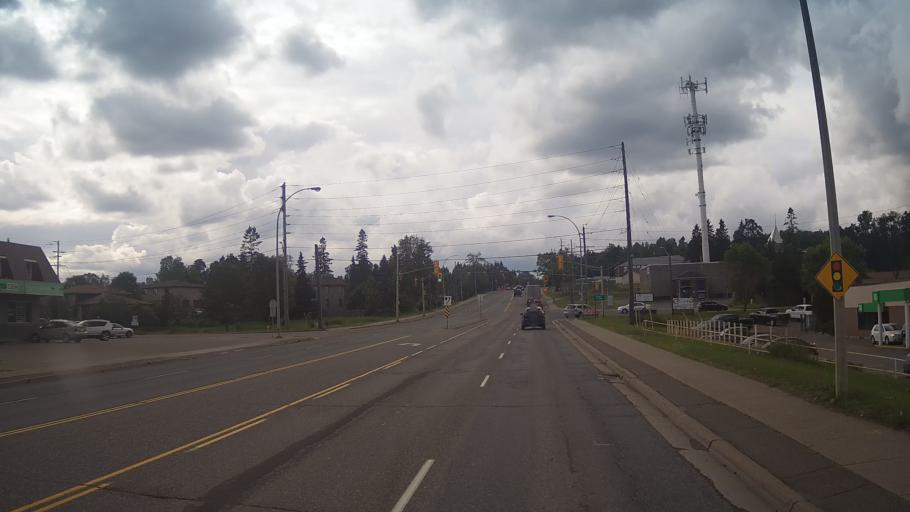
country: CA
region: Ontario
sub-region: Thunder Bay District
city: Thunder Bay
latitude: 48.4522
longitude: -89.2556
